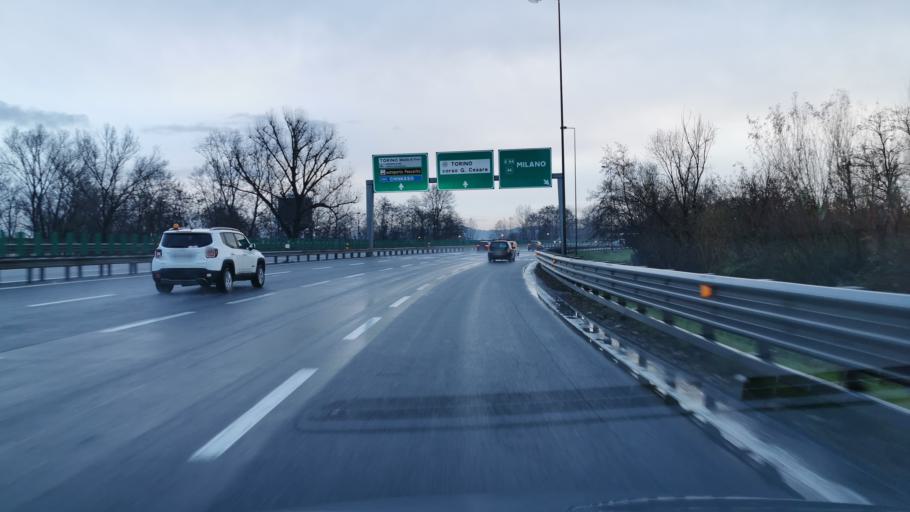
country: IT
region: Piedmont
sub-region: Provincia di Torino
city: Settimo Torinese
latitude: 45.1360
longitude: 7.7209
